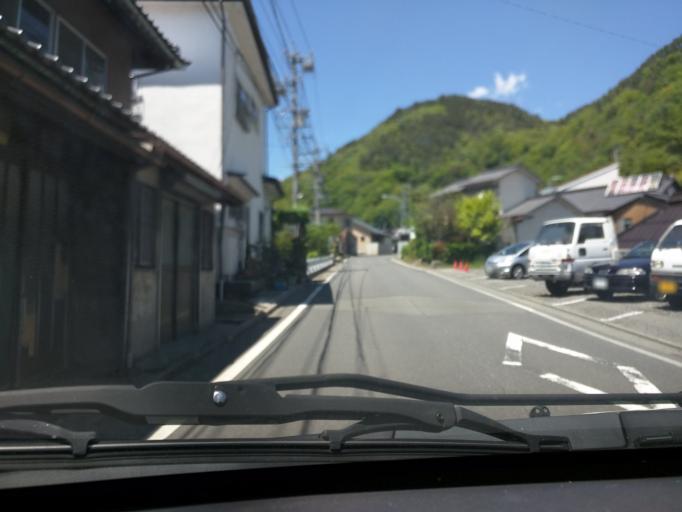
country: JP
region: Nagano
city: Nagano-shi
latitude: 36.6593
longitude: 138.1742
